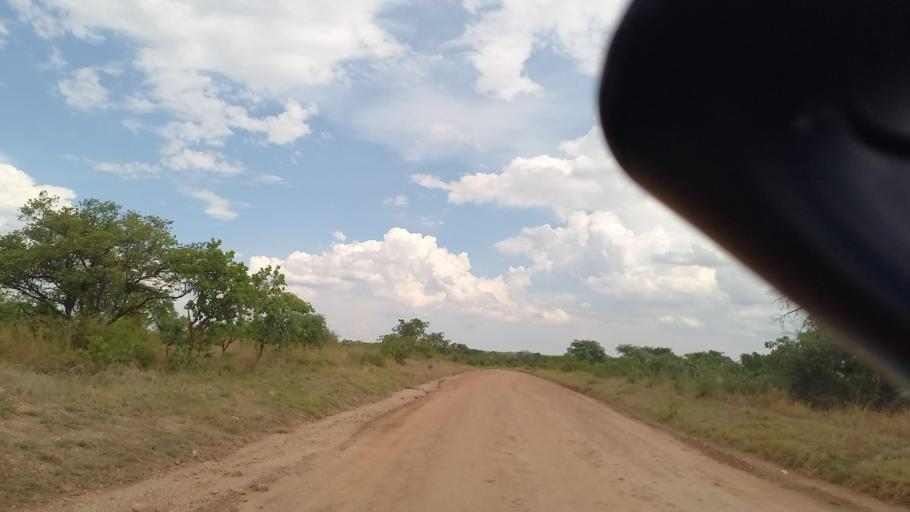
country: ZM
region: Southern
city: Nakambala
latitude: -16.0614
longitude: 27.9929
